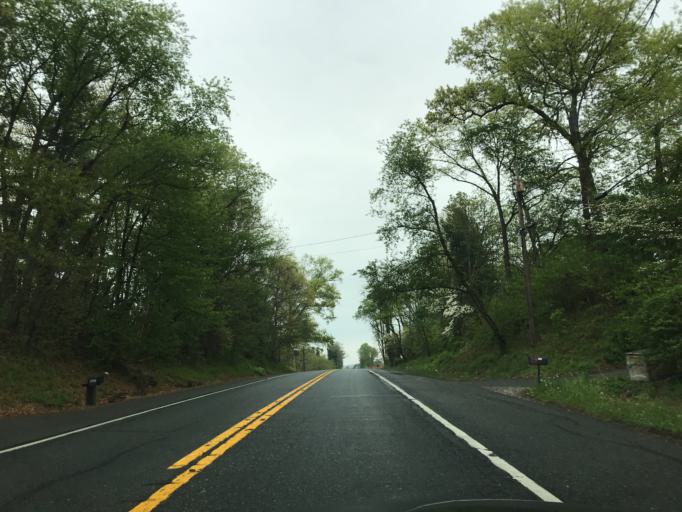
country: US
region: Maryland
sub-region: Harford County
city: Jarrettsville
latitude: 39.6674
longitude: -76.4177
